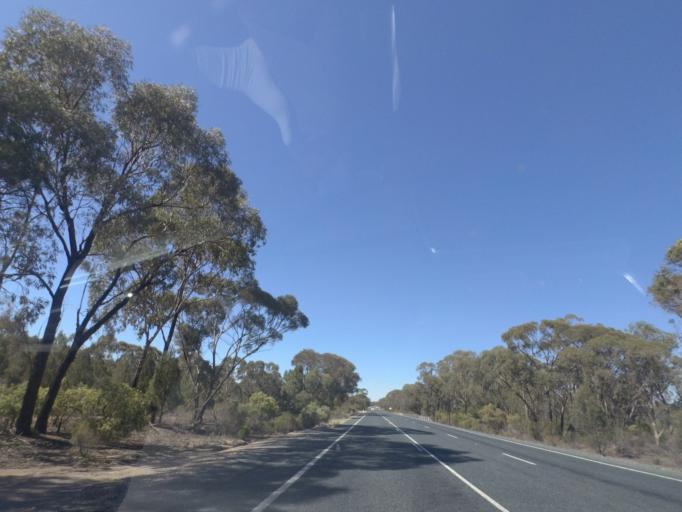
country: AU
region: New South Wales
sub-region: Bland
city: West Wyalong
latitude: -34.1313
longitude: 147.1234
